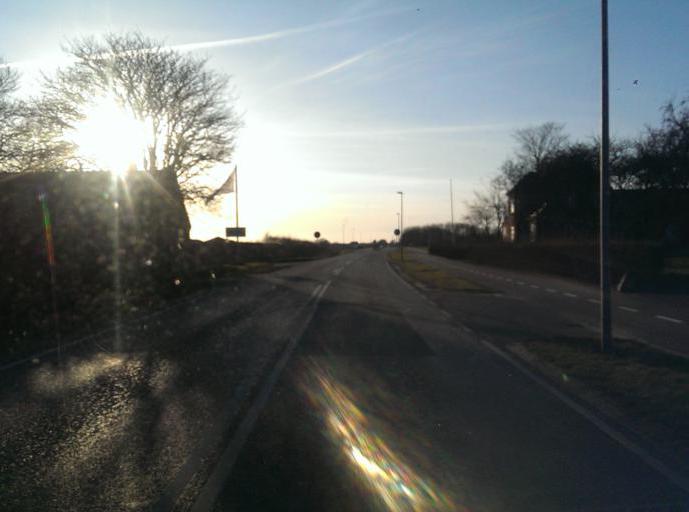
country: DK
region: South Denmark
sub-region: Esbjerg Kommune
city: Esbjerg
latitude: 55.5288
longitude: 8.4220
